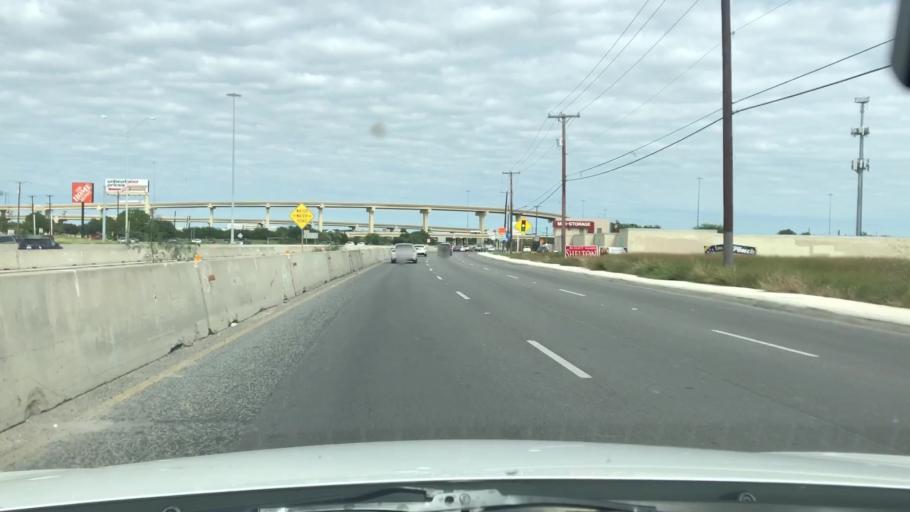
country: US
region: Texas
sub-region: Bexar County
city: Lackland Air Force Base
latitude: 29.4295
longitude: -98.6485
